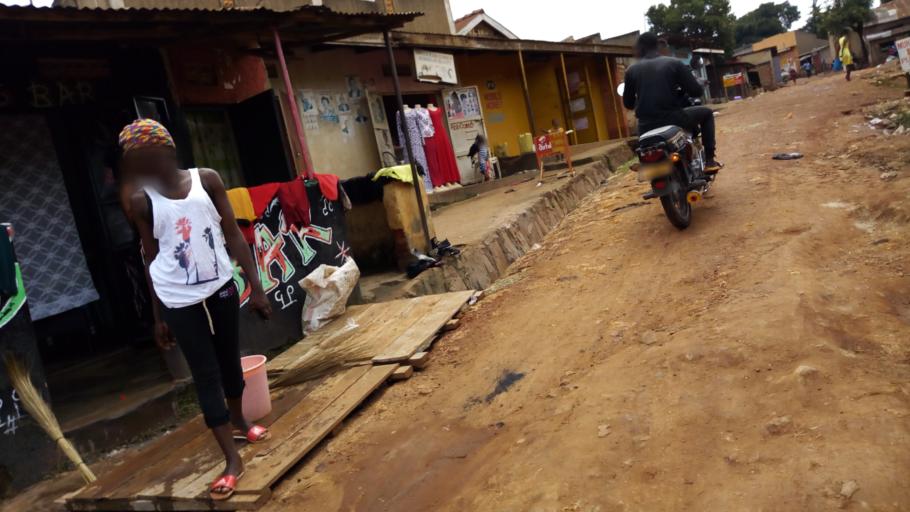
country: UG
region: Central Region
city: Kampala Central Division
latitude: 0.3787
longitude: 32.5604
